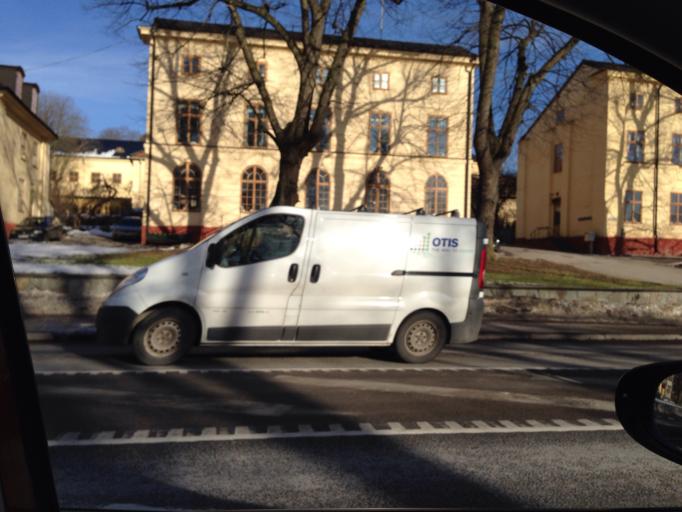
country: SE
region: Stockholm
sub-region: Stockholms Kommun
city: Bromma
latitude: 59.3242
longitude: 17.8879
